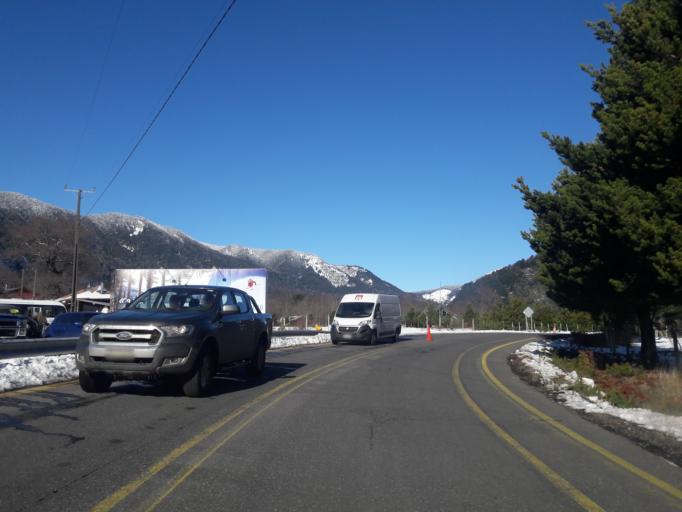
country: CL
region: Araucania
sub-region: Provincia de Cautin
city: Vilcun
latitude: -38.4785
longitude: -71.5367
